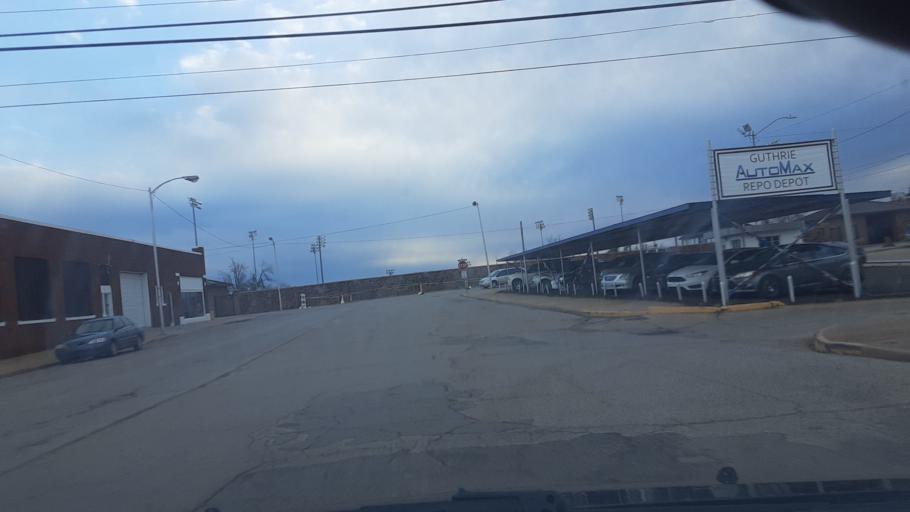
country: US
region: Oklahoma
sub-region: Logan County
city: Guthrie
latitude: 35.8777
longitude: -97.4241
